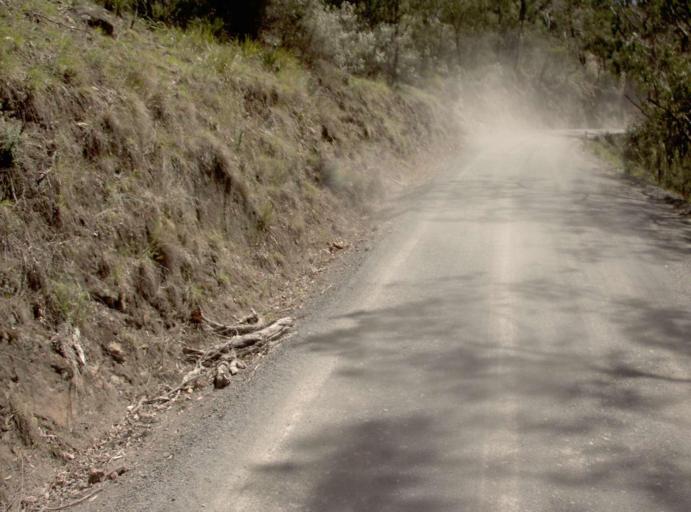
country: AU
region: New South Wales
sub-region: Bombala
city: Bombala
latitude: -37.0999
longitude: 148.6304
